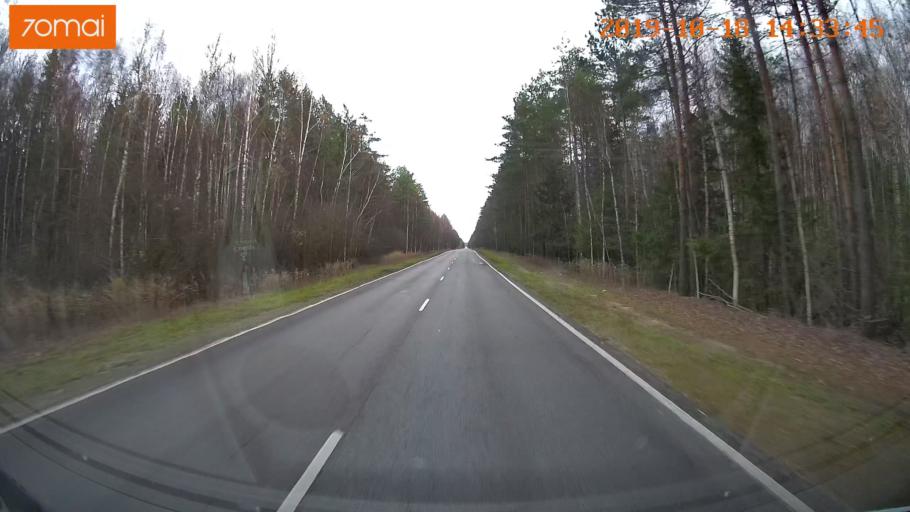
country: RU
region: Rjazan
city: Tuma
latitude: 55.2049
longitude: 40.6029
